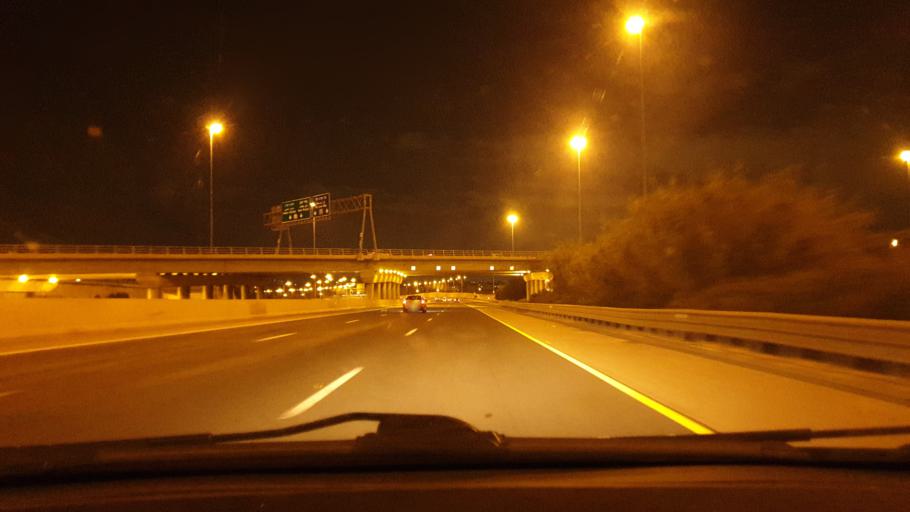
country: IL
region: Central District
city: Ness Ziona
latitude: 31.9381
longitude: 34.8162
